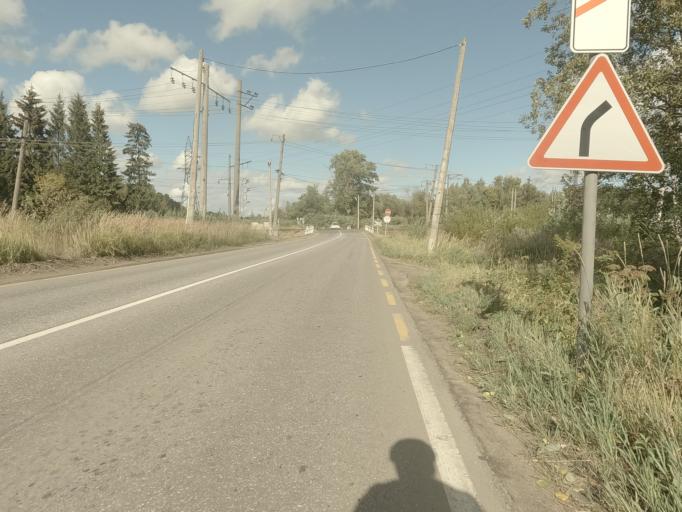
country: RU
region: Leningrad
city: Romanovka
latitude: 60.0240
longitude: 30.6987
